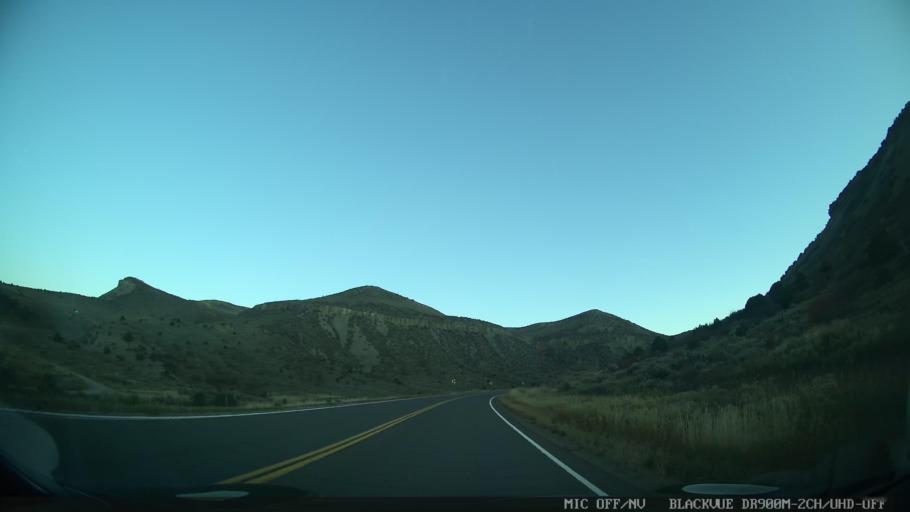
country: US
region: Colorado
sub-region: Eagle County
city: Edwards
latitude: 39.7721
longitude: -106.6828
